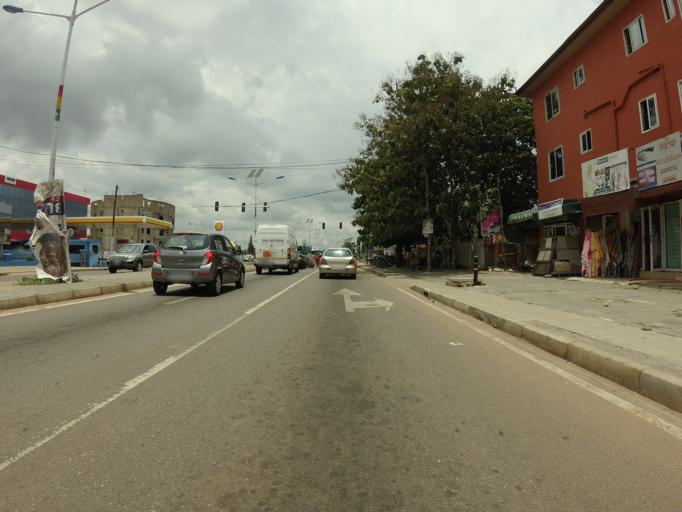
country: GH
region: Greater Accra
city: Medina Estates
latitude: 5.6502
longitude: -0.1505
